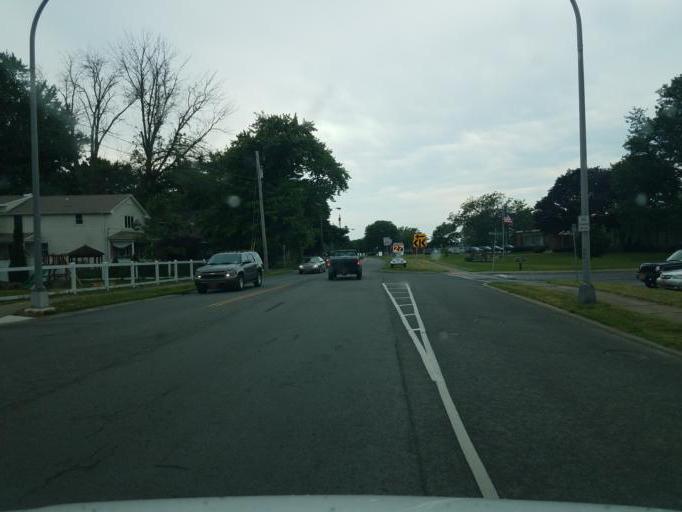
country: US
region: New York
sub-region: Erie County
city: Tonawanda
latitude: 43.0191
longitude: -78.8853
